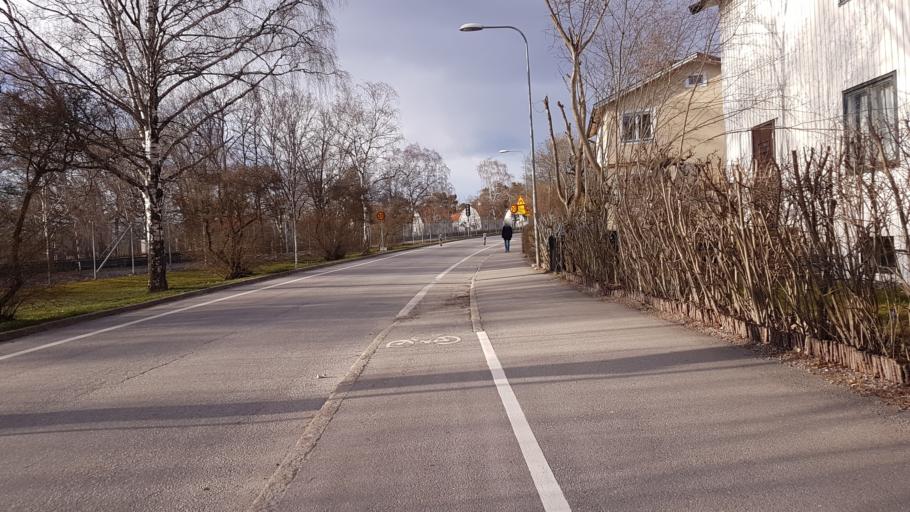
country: SE
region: Stockholm
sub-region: Stockholms Kommun
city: Arsta
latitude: 59.2902
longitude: 18.0702
